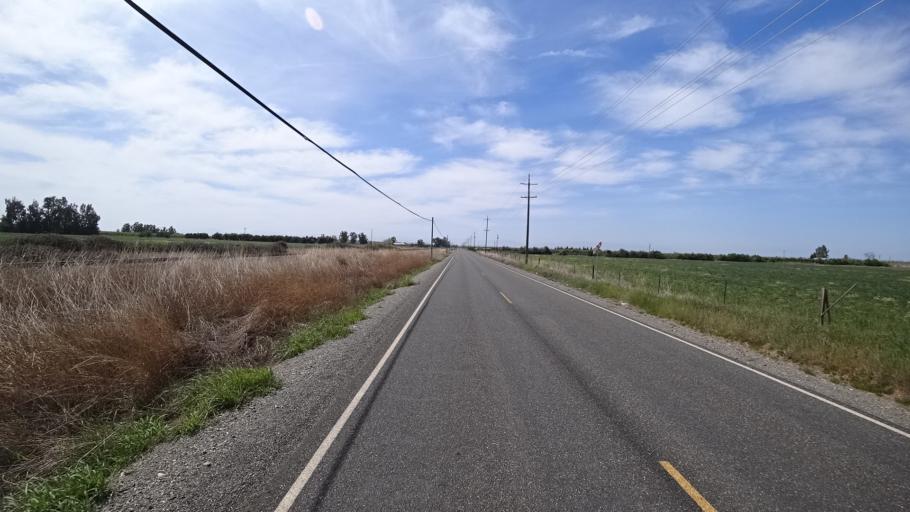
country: US
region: California
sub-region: Glenn County
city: Orland
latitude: 39.7685
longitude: -122.1202
